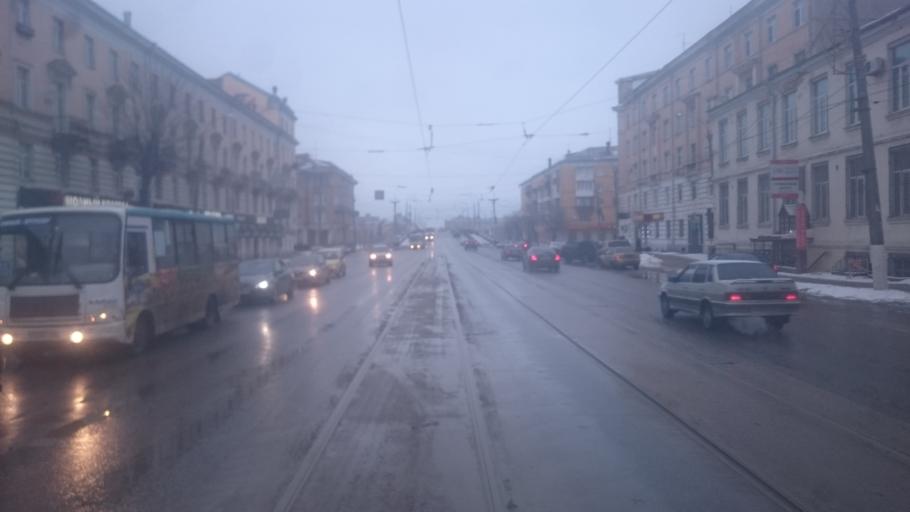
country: RU
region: Tverskaya
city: Tver
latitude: 56.8603
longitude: 35.9092
